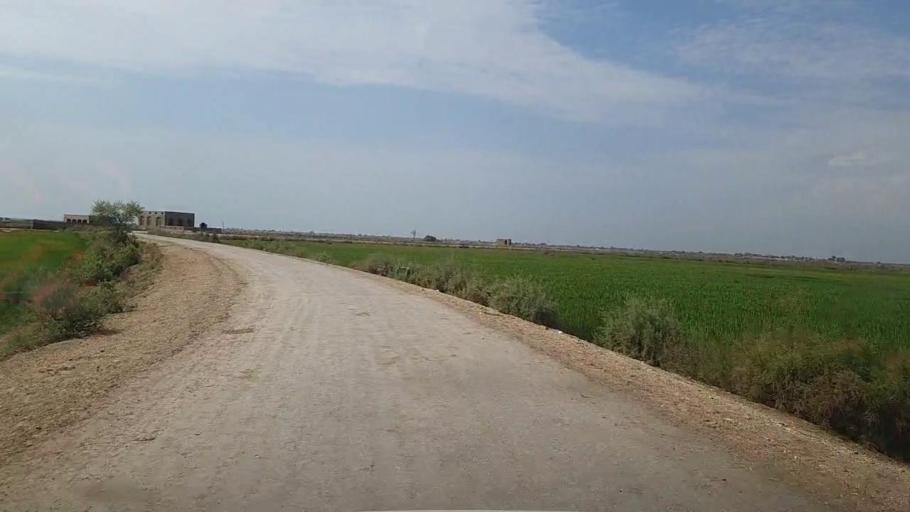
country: PK
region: Sindh
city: Thul
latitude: 28.2747
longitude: 68.8225
